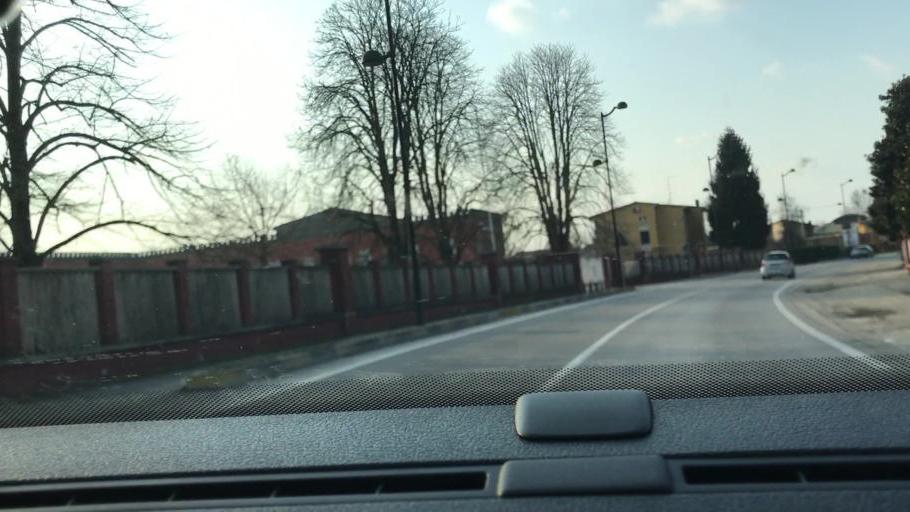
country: IT
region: Emilia-Romagna
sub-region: Provincia di Parma
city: Mezzano Inferiore
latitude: 44.9424
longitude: 10.4799
